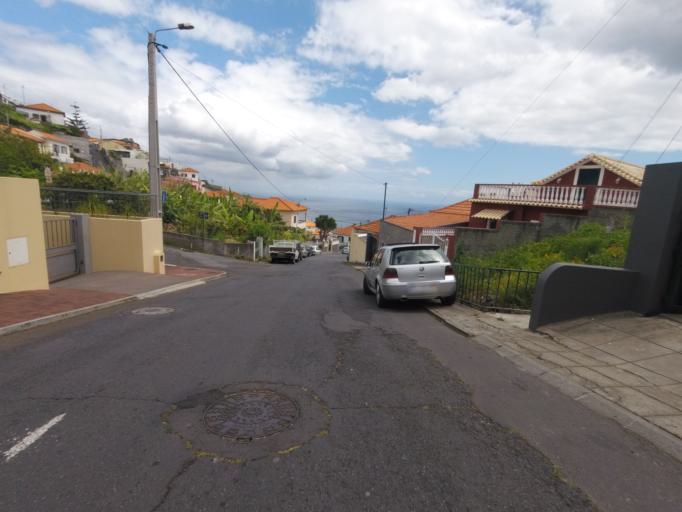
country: PT
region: Madeira
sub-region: Funchal
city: Nossa Senhora do Monte
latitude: 32.6647
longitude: -16.9151
